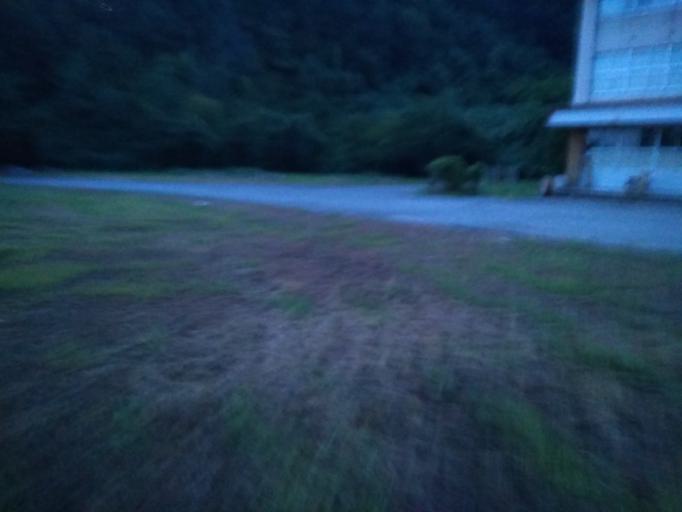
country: JP
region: Akita
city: Kakunodatemachi
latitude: 39.5967
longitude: 140.5713
